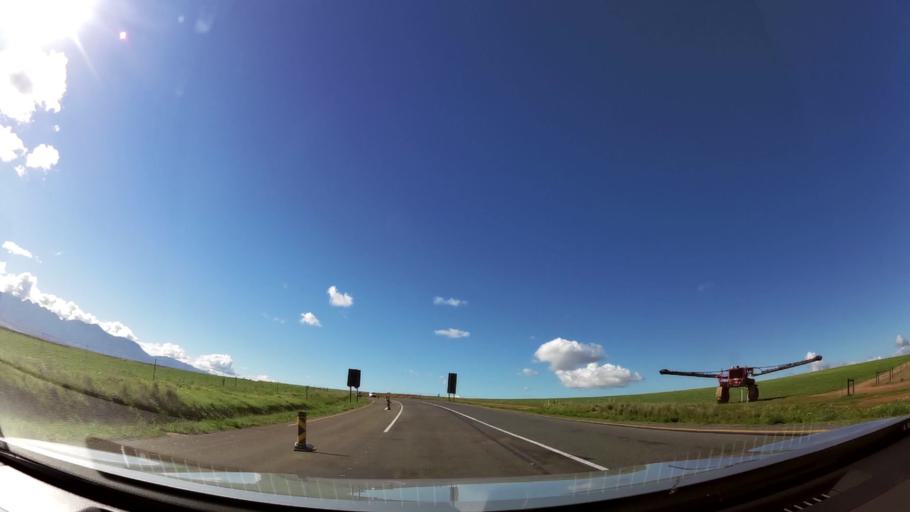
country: ZA
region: Western Cape
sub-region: Overberg District Municipality
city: Caledon
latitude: -34.1846
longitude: 19.6819
